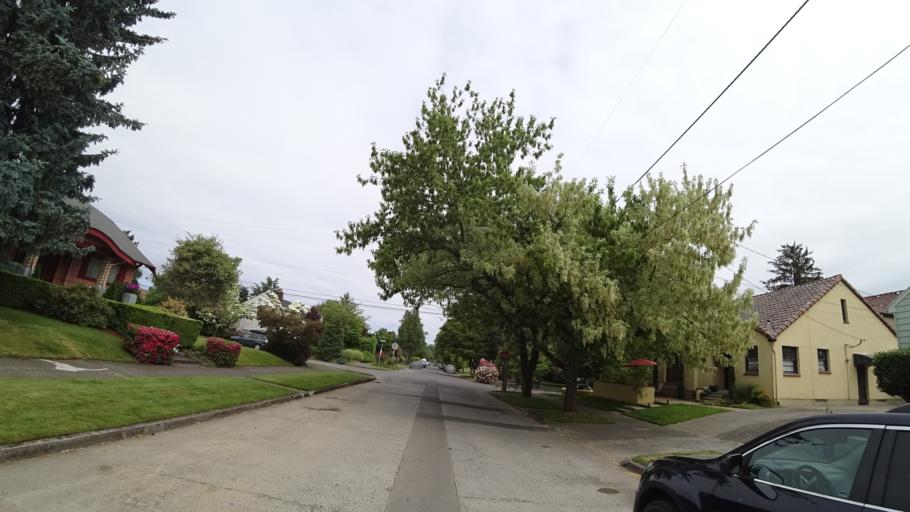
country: US
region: Oregon
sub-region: Multnomah County
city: Portland
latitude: 45.5679
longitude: -122.6392
